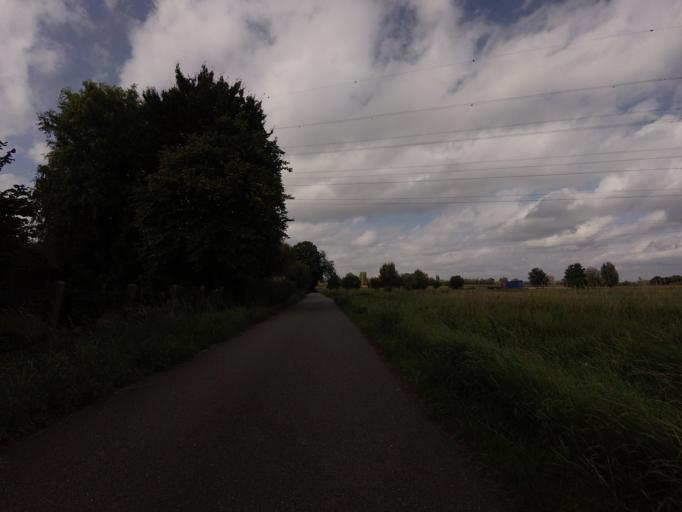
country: BE
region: Flanders
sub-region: Provincie Antwerpen
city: Aartselaar
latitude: 51.1158
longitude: 4.3769
